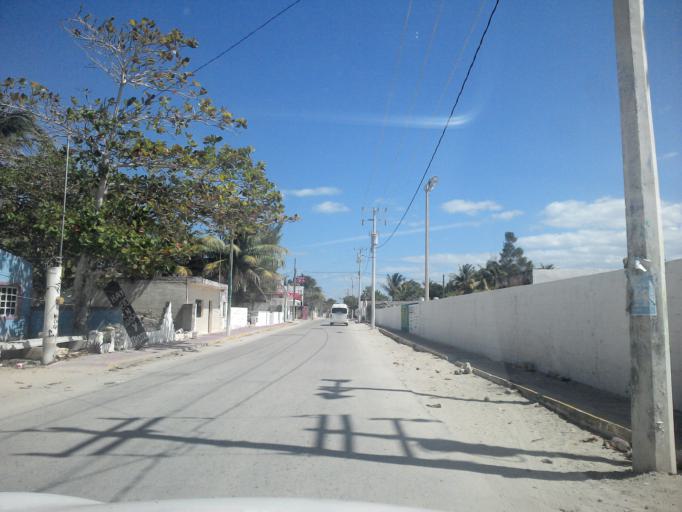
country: MX
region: Yucatan
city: Telchac Puerto
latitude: 21.3417
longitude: -89.2724
